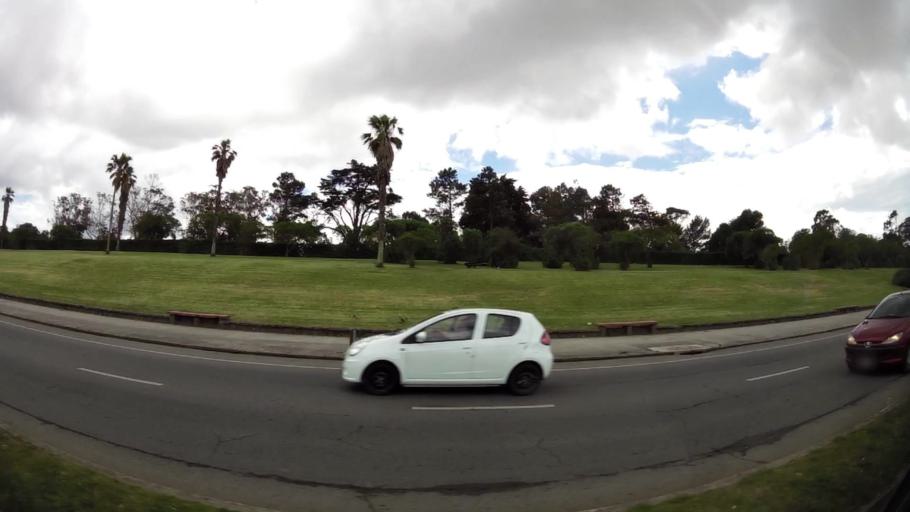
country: UY
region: Montevideo
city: Montevideo
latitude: -34.9253
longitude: -56.1677
